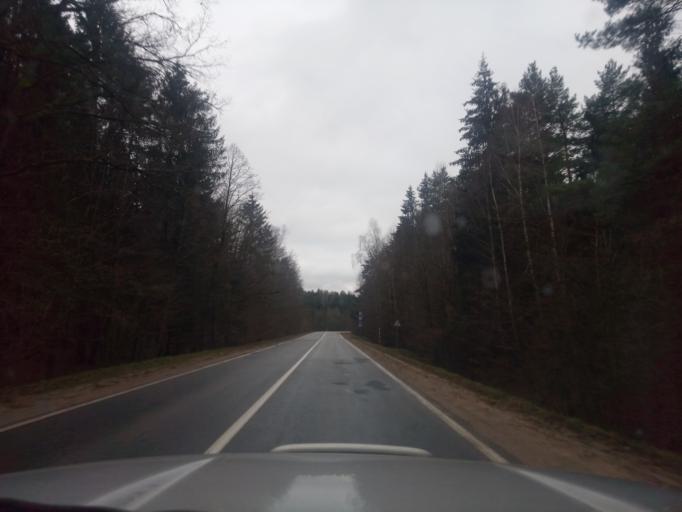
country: BY
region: Minsk
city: Kapyl'
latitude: 53.1620
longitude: 27.1163
